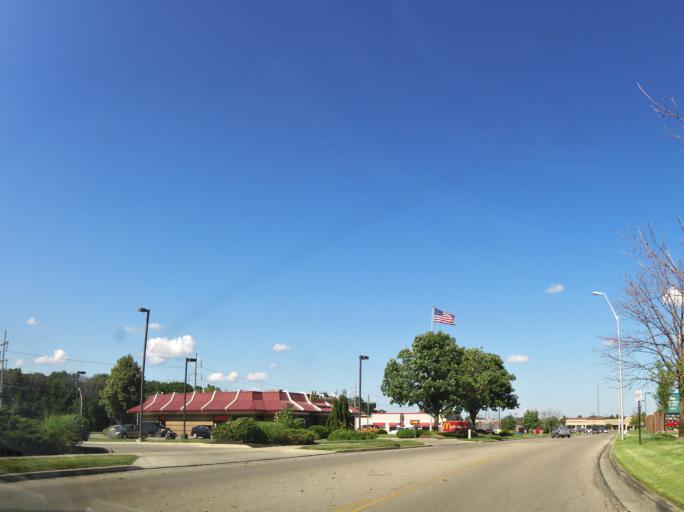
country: US
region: Ohio
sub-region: Greene County
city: Wright-Patterson AFB
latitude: 39.7775
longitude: -84.0577
